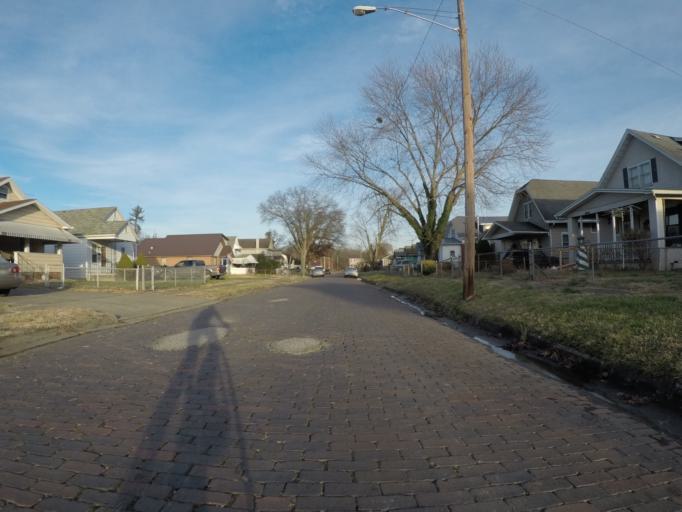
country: US
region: Ohio
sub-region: Lawrence County
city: Burlington
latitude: 38.4013
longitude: -82.4993
